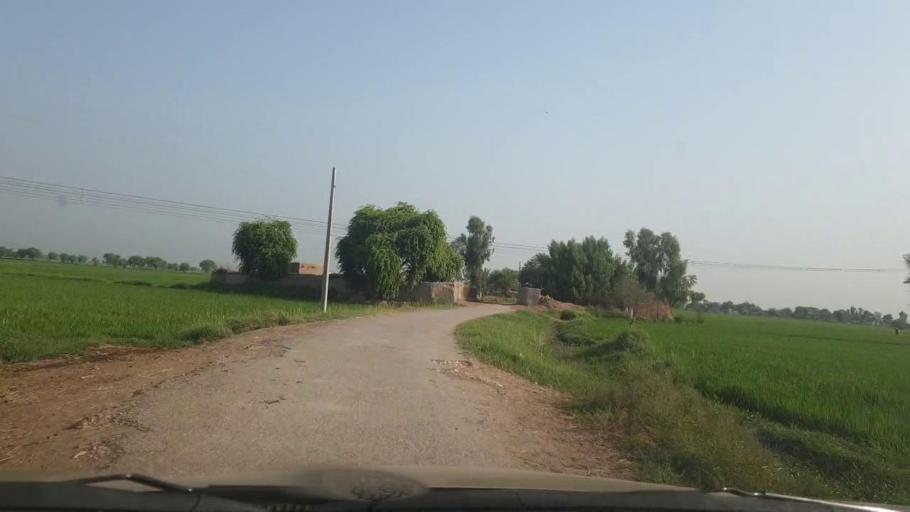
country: PK
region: Sindh
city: Larkana
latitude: 27.5905
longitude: 68.1605
